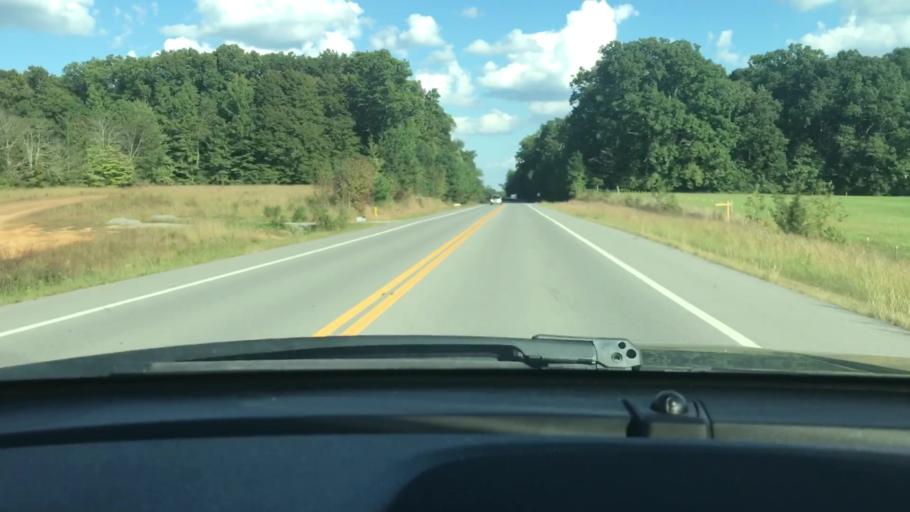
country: US
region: Tennessee
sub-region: Sumner County
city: White House
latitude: 36.4601
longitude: -86.6584
